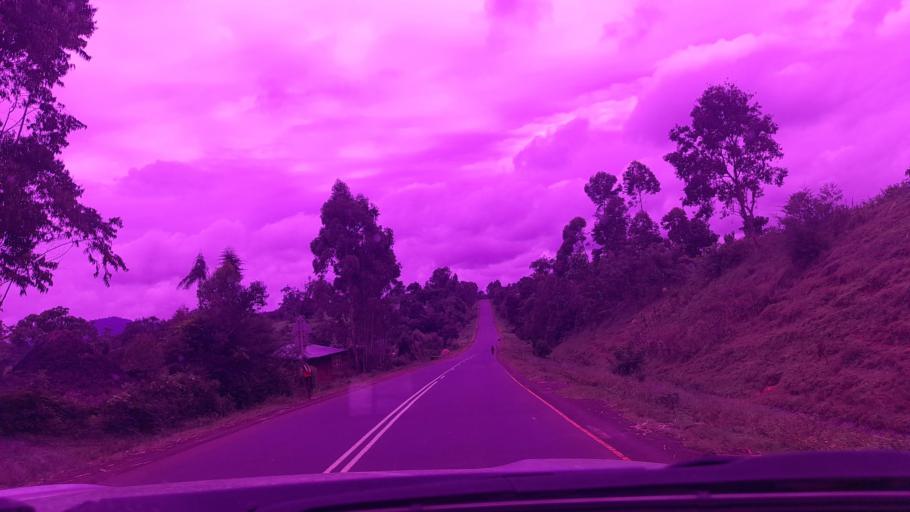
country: ET
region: Southern Nations, Nationalities, and People's Region
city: Bonga
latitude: 7.3055
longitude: 35.9962
